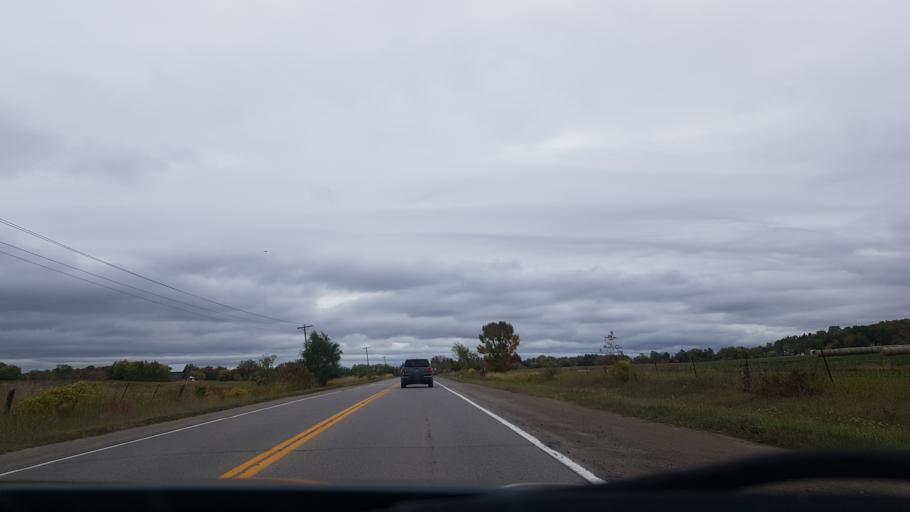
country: CA
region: Ontario
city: Omemee
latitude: 44.2306
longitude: -78.4821
